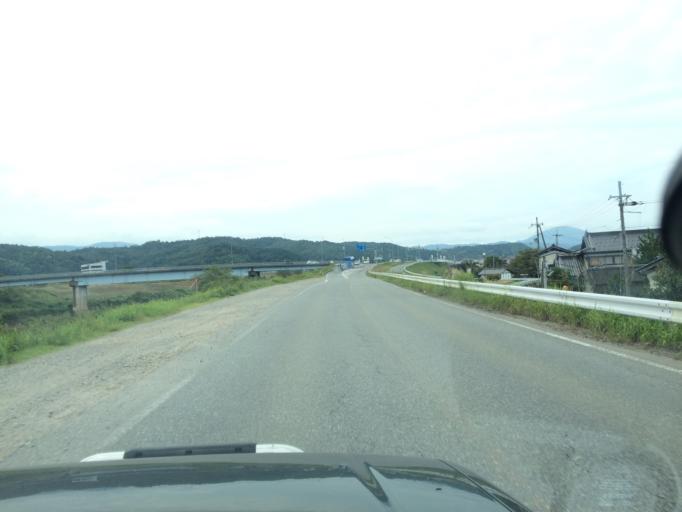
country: JP
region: Hyogo
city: Toyooka
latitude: 35.5119
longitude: 134.8281
